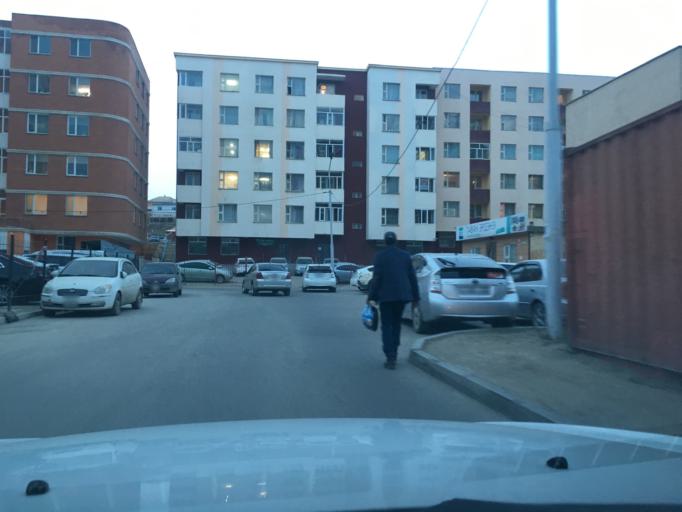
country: MN
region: Ulaanbaatar
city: Ulaanbaatar
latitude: 47.9170
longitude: 106.8599
